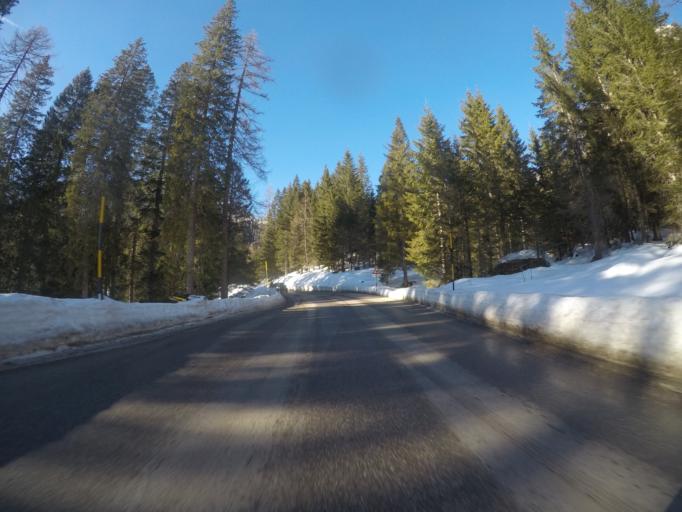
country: IT
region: Trentino-Alto Adige
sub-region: Provincia di Trento
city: Siror
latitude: 46.2712
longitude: 11.8021
